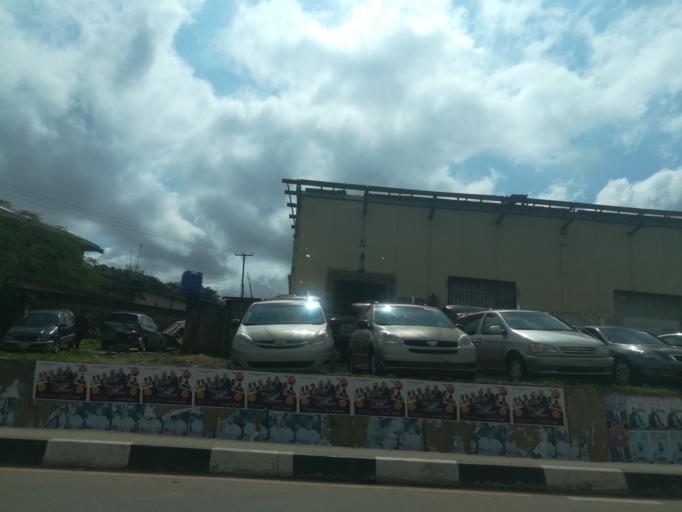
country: NG
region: Oyo
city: Ibadan
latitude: 7.3327
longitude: 3.8688
